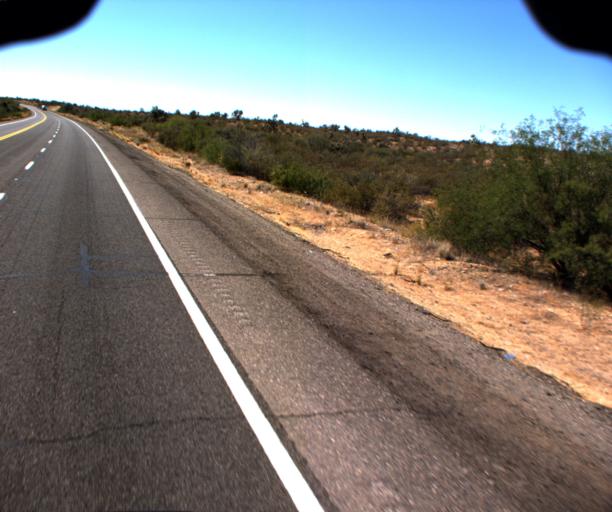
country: US
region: Arizona
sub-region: Yavapai County
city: Congress
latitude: 34.1995
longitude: -113.0608
